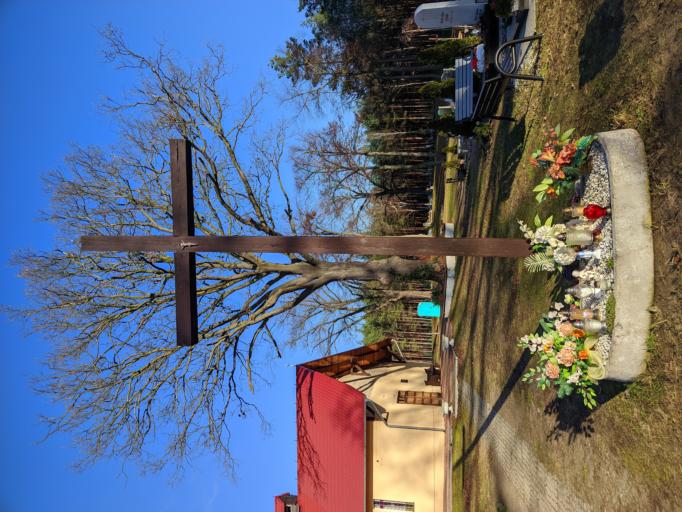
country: PL
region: Lubusz
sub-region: Powiat nowosolski
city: Przyborow
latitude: 51.8046
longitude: 15.7691
